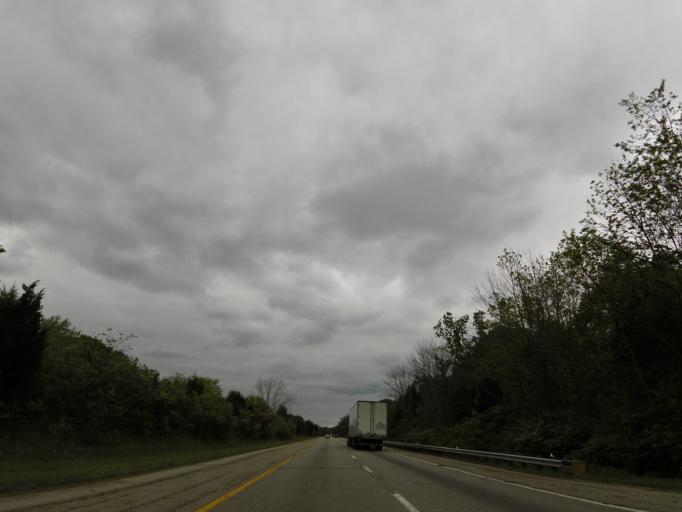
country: US
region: Ohio
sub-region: Warren County
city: South Lebanon
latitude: 39.3947
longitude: -84.1932
